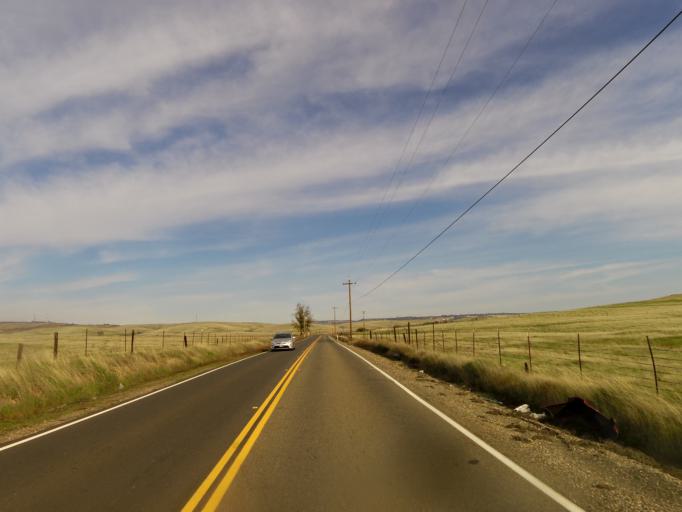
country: US
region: California
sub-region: El Dorado County
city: El Dorado Hills
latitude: 38.6206
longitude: -121.1186
